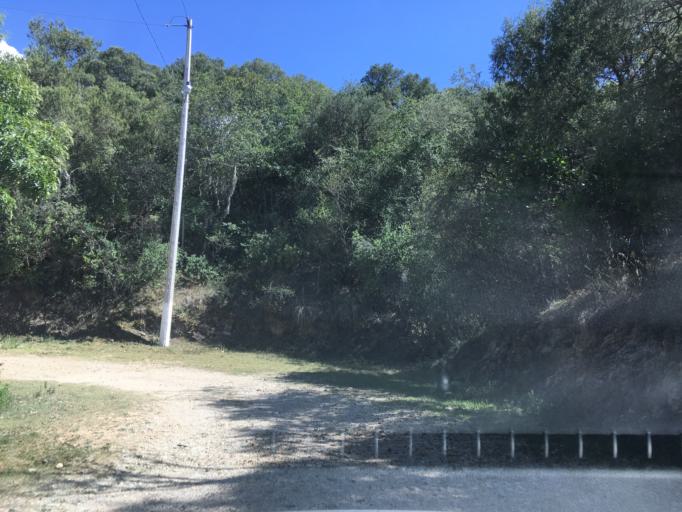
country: MX
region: Hidalgo
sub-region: Omitlan de Juarez
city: San Antonio el Paso
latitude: 20.2347
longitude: -98.5675
